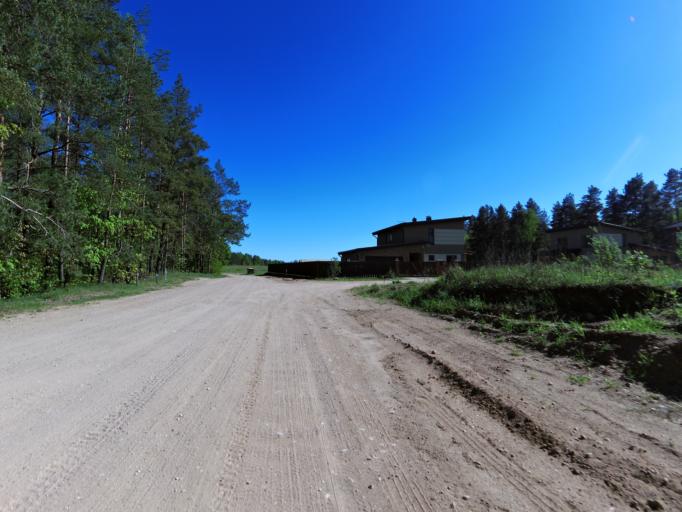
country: LT
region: Vilnius County
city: Pilaite
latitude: 54.6918
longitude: 25.1586
